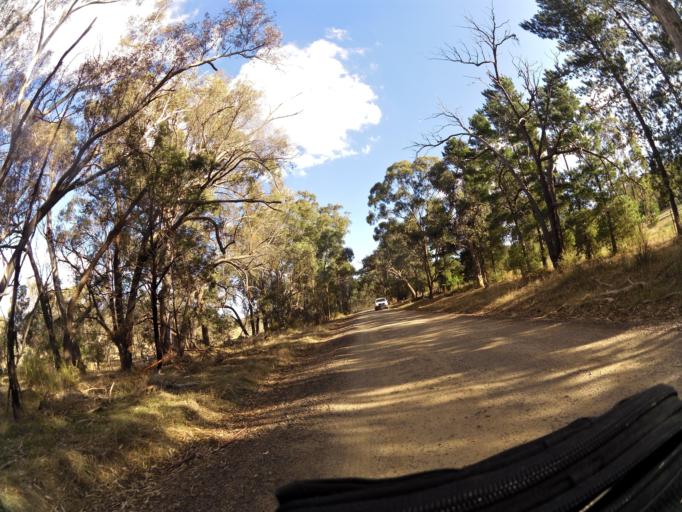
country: AU
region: Victoria
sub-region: Greater Bendigo
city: Kennington
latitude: -37.0129
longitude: 144.8086
